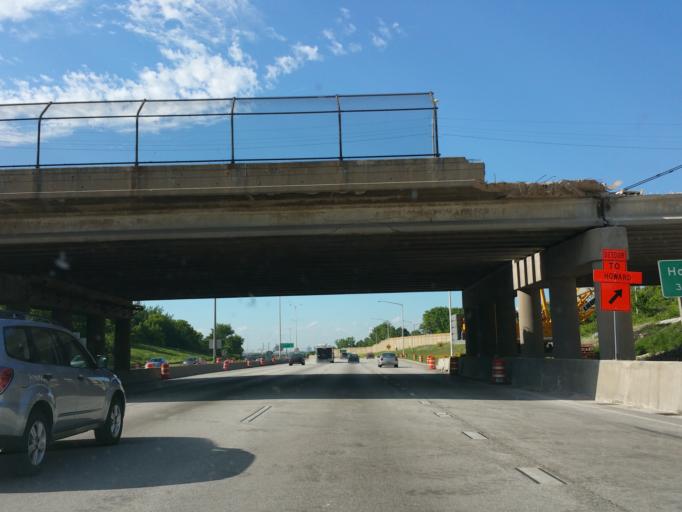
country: US
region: Wisconsin
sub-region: Milwaukee County
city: Saint Francis
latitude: 42.9735
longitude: -87.9154
